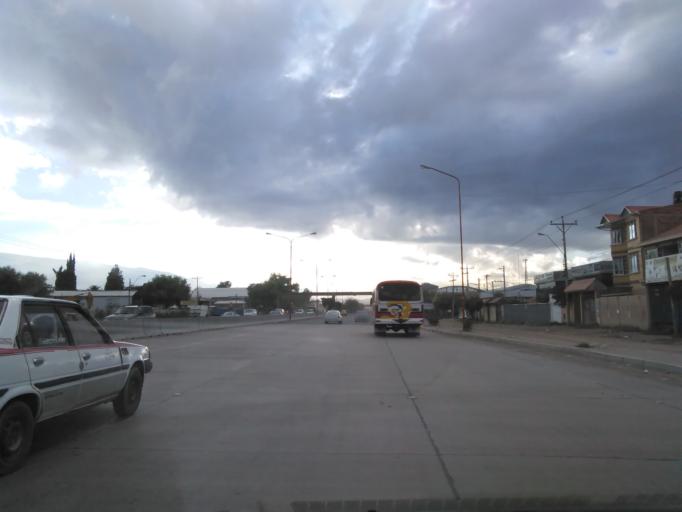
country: BO
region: Cochabamba
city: Cochabamba
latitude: -17.3914
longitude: -66.2296
